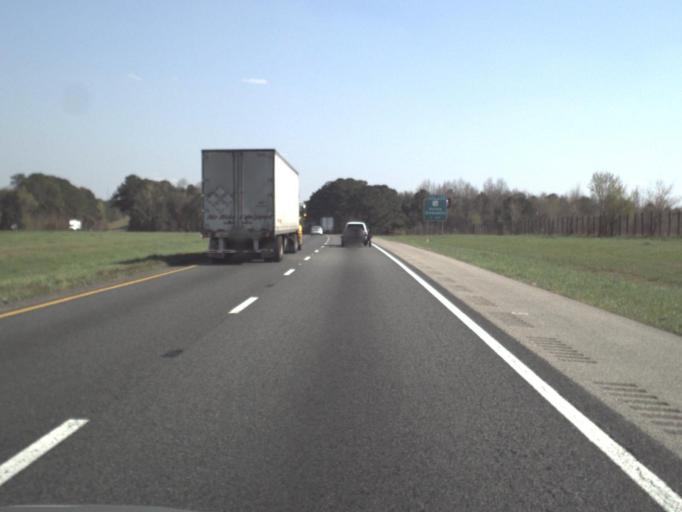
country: US
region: Florida
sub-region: Gadsden County
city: Gretna
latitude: 30.5892
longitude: -84.7190
